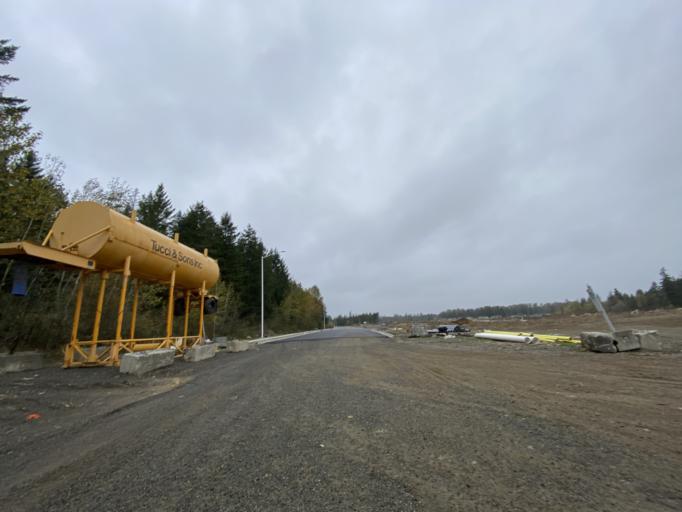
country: US
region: Washington
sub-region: Pierce County
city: South Hill
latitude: 47.0917
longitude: -122.2570
